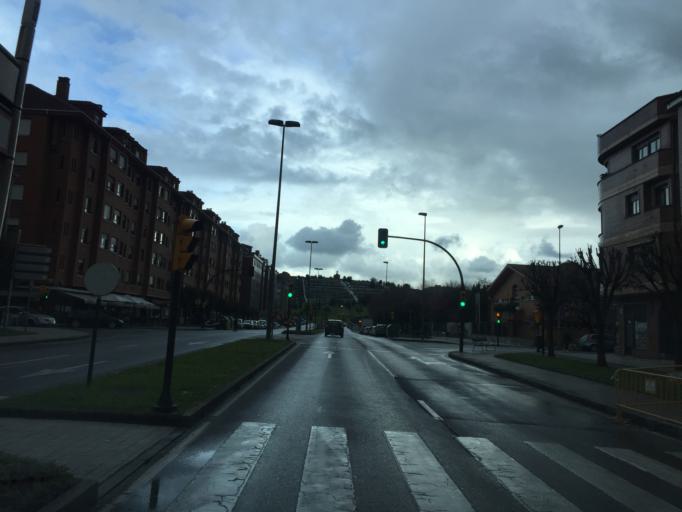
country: ES
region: Asturias
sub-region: Province of Asturias
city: Gijon
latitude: 43.5258
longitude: -5.6675
